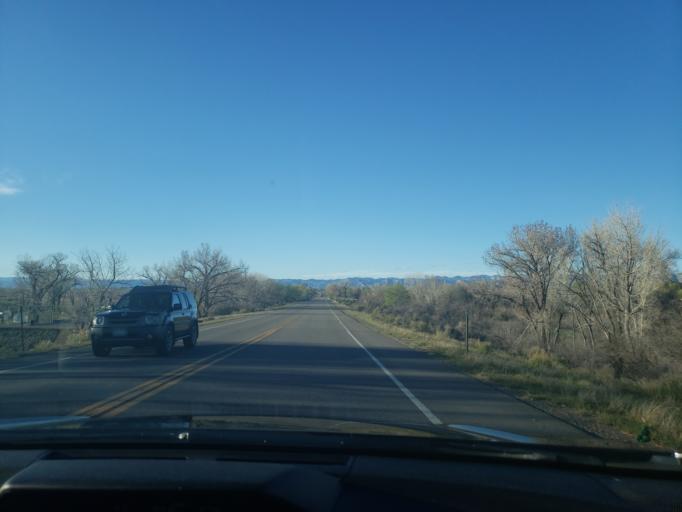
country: US
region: Colorado
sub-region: Mesa County
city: Fruita
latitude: 39.1388
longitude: -108.7383
